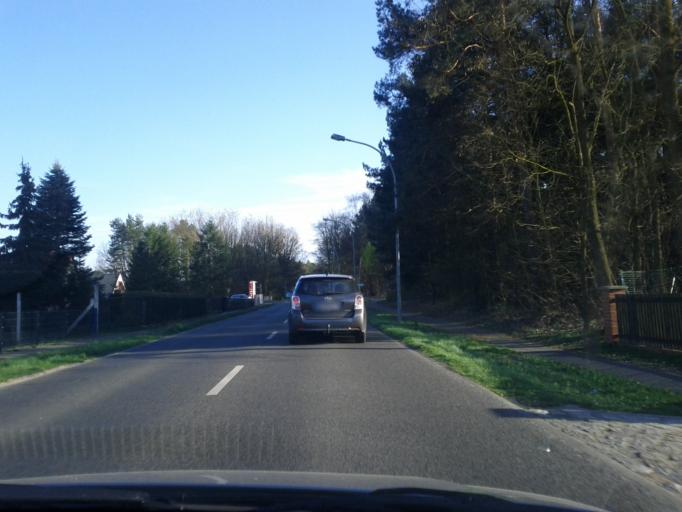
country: DE
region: Brandenburg
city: Langewahl
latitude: 52.3281
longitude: 14.0782
